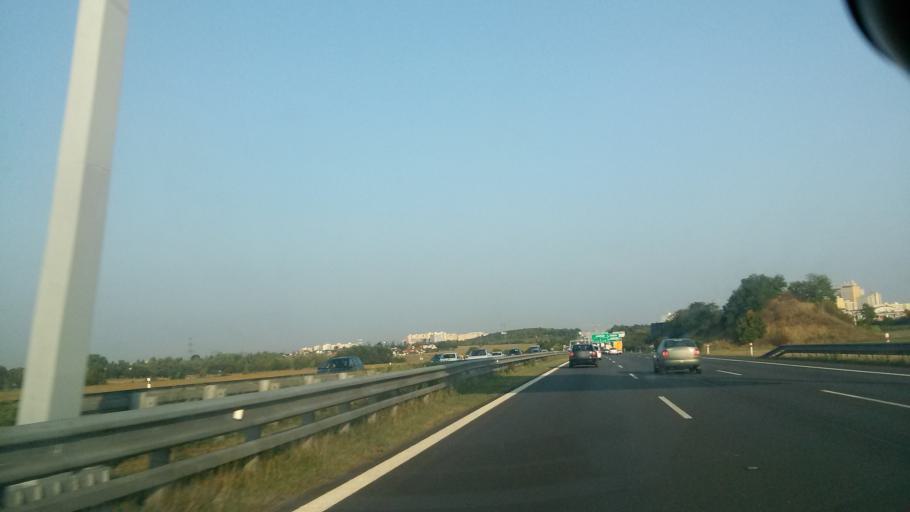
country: CZ
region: Central Bohemia
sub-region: Okres Praha-Zapad
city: Pruhonice
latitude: 50.0150
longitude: 14.5280
